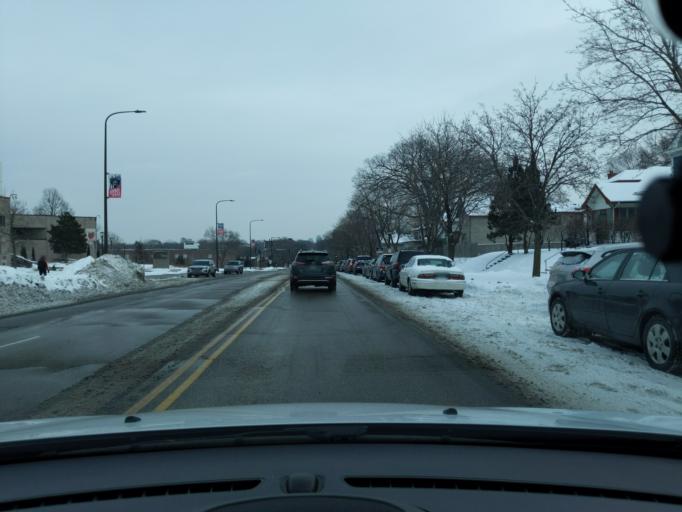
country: US
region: Minnesota
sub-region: Ramsey County
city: Falcon Heights
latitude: 44.9486
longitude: -93.1488
